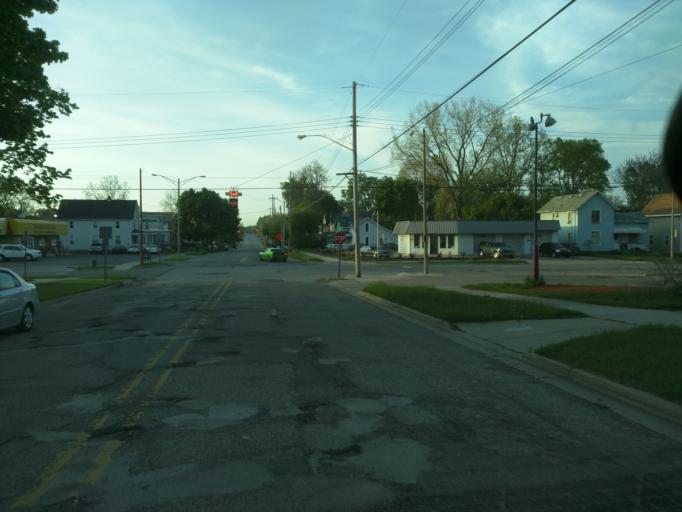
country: US
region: Michigan
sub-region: Ingham County
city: Lansing
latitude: 42.7470
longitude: -84.5553
